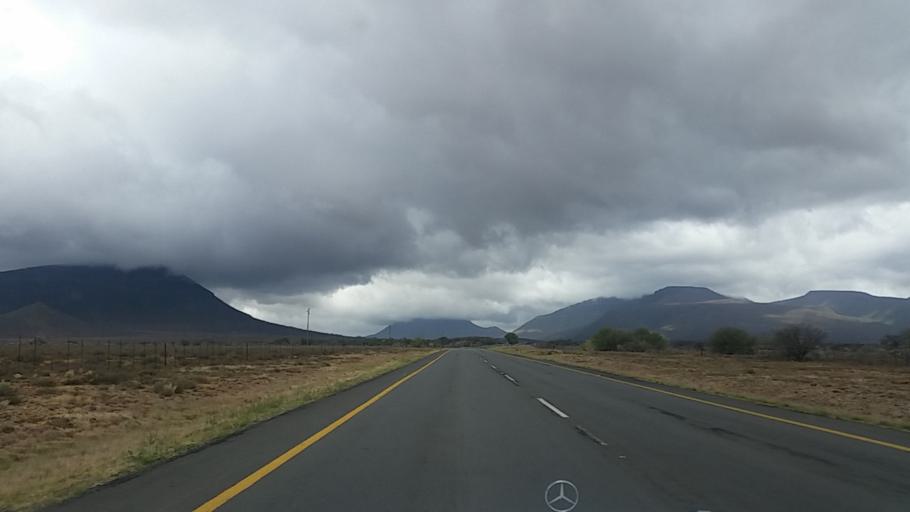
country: ZA
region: Eastern Cape
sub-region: Cacadu District Municipality
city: Graaff-Reinet
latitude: -32.2016
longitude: 24.5522
